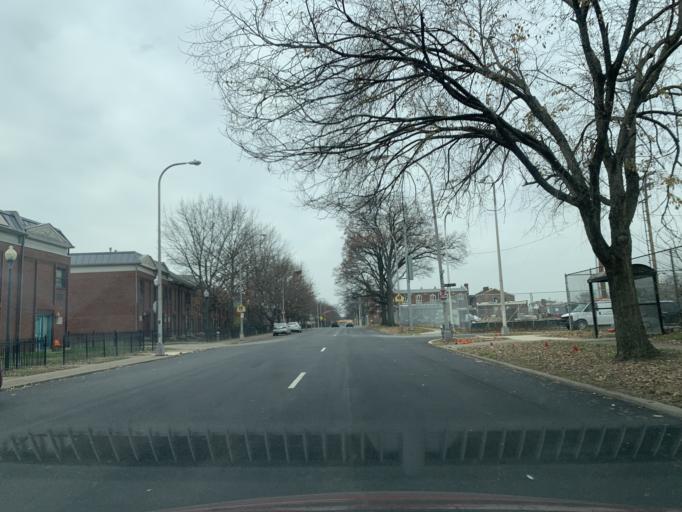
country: US
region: Kentucky
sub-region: Jefferson County
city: Louisville
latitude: 38.2522
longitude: -85.7669
